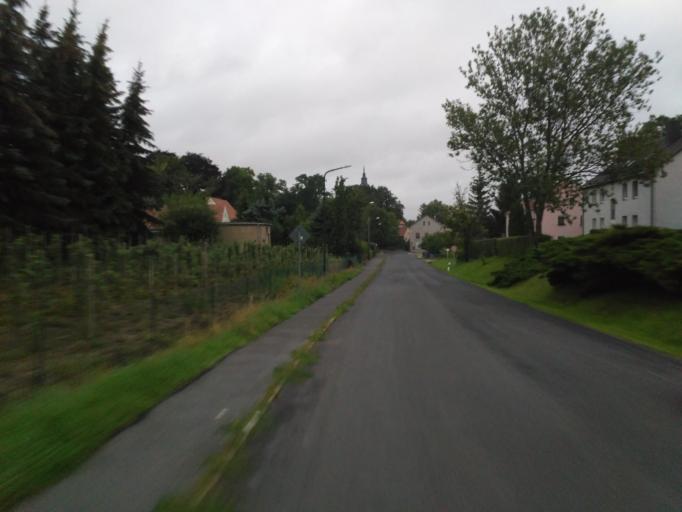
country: DE
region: Saxony
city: Nossen
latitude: 51.1179
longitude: 13.3775
